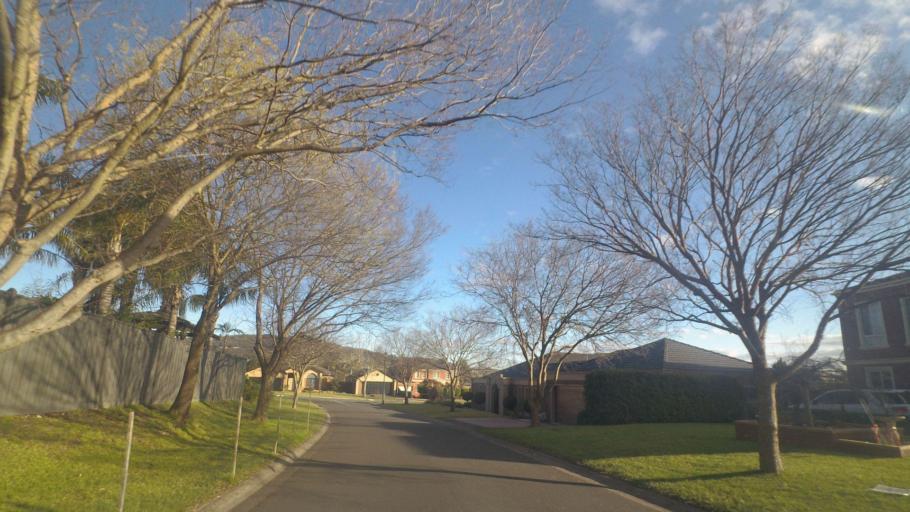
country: AU
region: Victoria
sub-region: Yarra Ranges
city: Lysterfield
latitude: -37.9141
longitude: 145.2853
